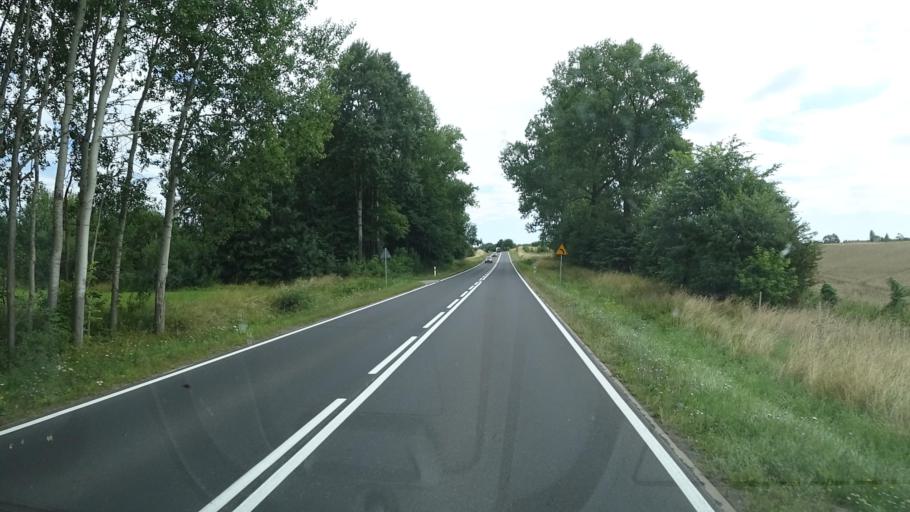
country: PL
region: Warmian-Masurian Voivodeship
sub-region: Powiat elcki
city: Stare Juchy
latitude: 53.7967
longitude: 22.2305
